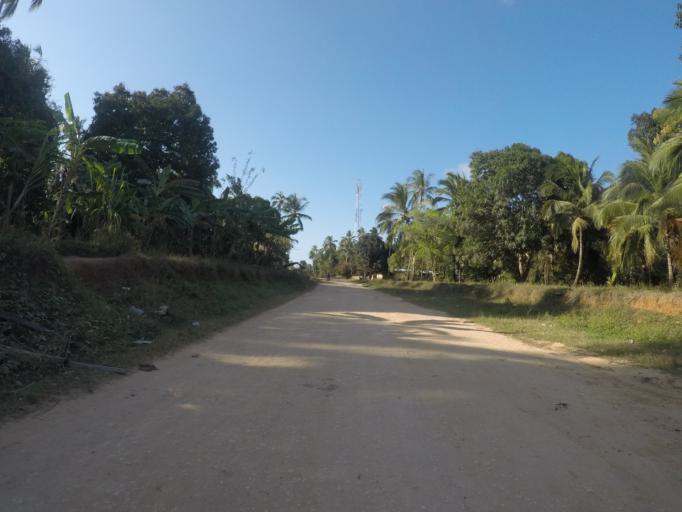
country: TZ
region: Zanzibar Central/South
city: Koani
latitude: -6.1607
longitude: 39.2872
